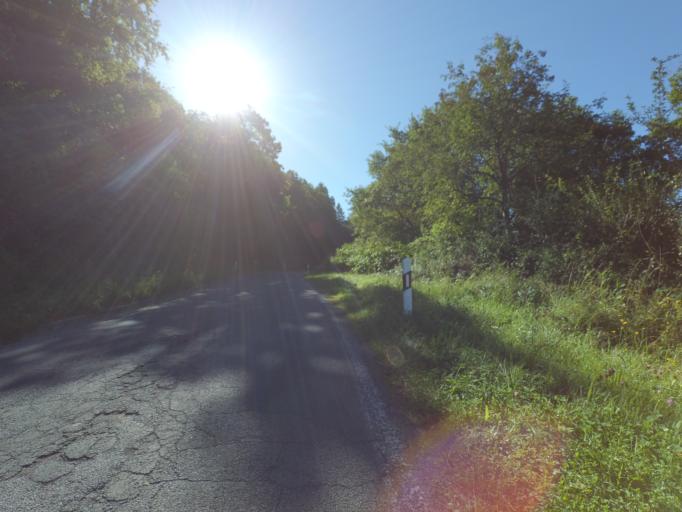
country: DE
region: Rheinland-Pfalz
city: Niederstadtfeld
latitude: 50.1726
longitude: 6.7760
